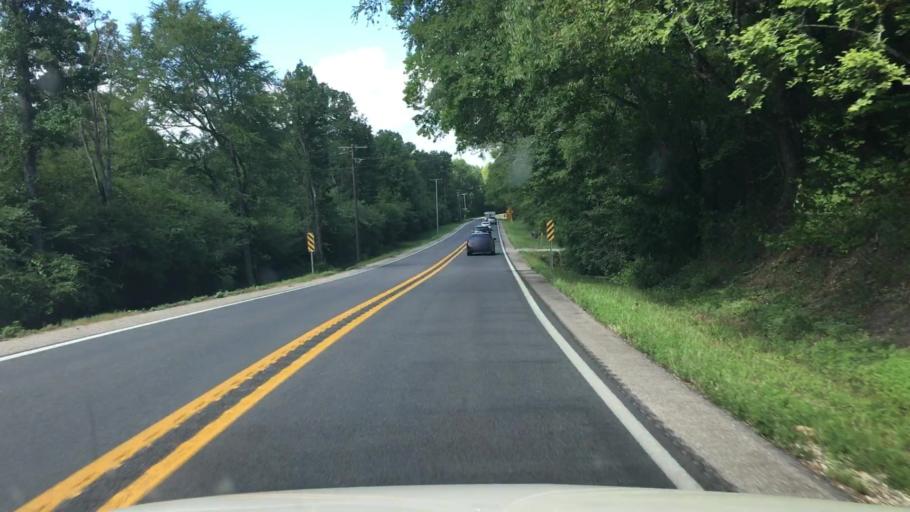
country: US
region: Arkansas
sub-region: Garland County
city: Lake Hamilton
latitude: 34.3865
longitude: -93.1231
